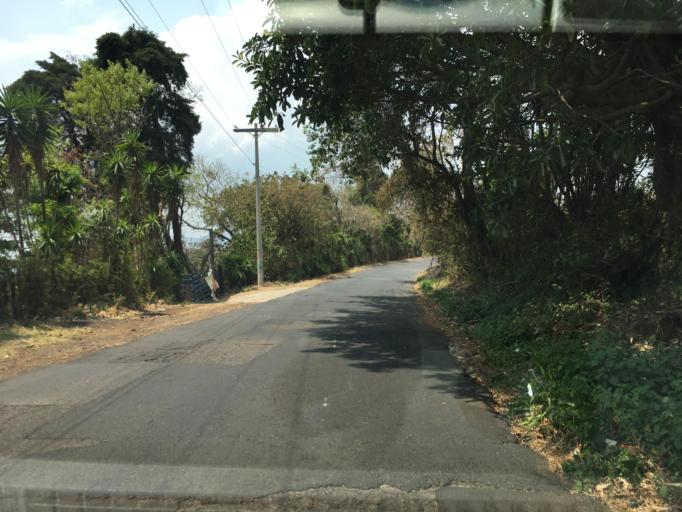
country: GT
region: Escuintla
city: San Vicente Pacaya
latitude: 14.3784
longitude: -90.5530
